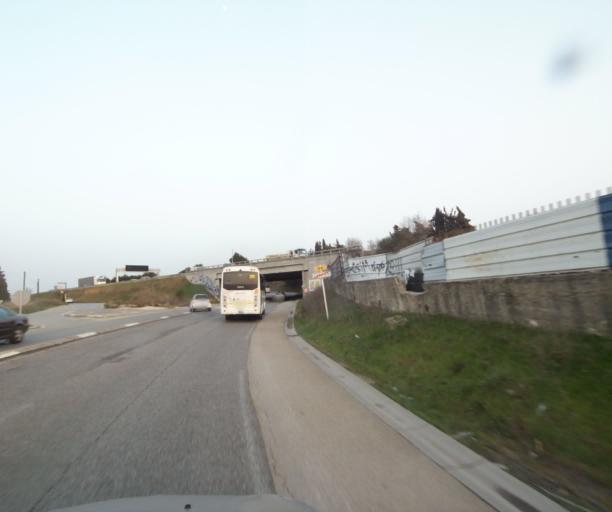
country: FR
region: Provence-Alpes-Cote d'Azur
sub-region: Departement des Bouches-du-Rhone
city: Cabries
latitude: 43.4228
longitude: 5.3713
